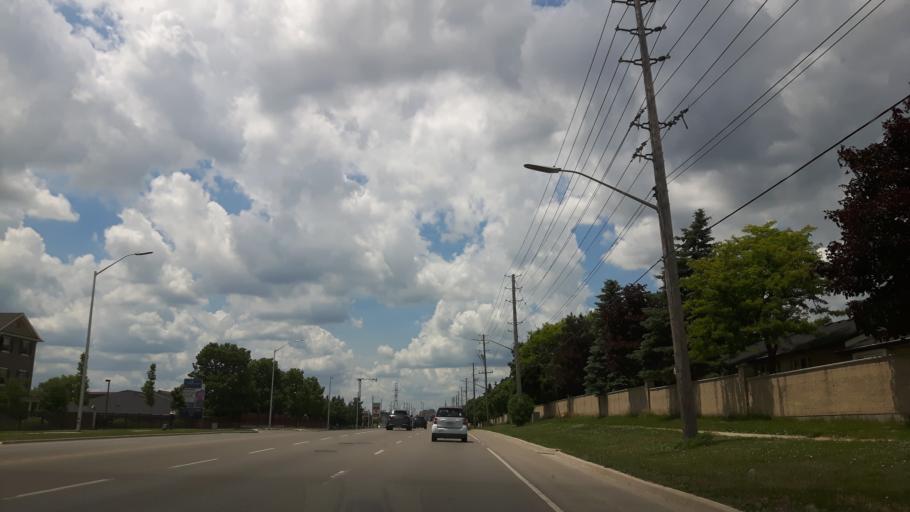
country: CA
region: Ontario
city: London
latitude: 42.9396
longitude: -81.2755
